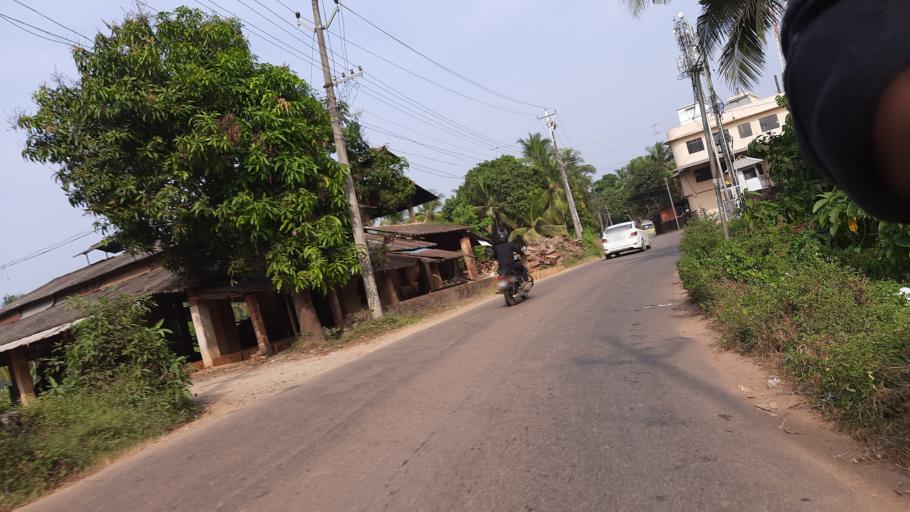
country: IN
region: Kerala
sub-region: Kozhikode
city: Ferokh
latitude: 11.1998
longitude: 75.8648
